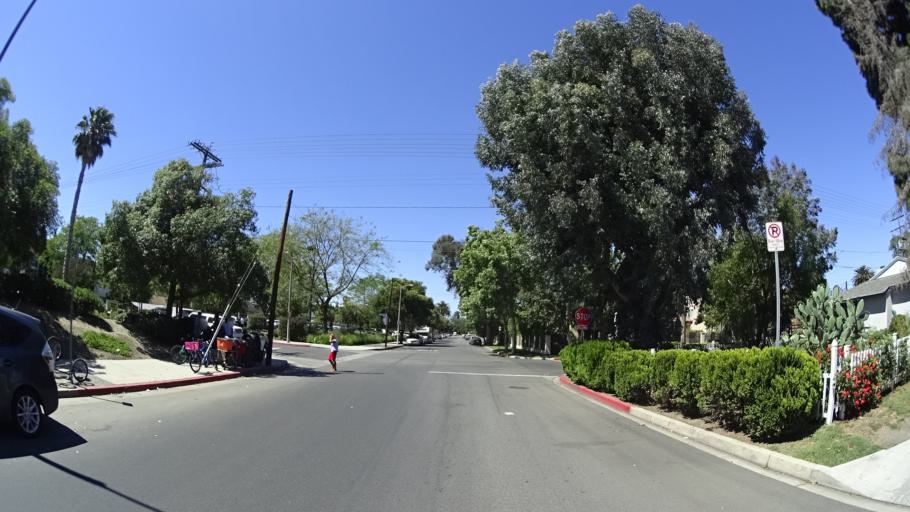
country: US
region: California
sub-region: Los Angeles County
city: Sherman Oaks
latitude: 34.1527
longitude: -118.4465
